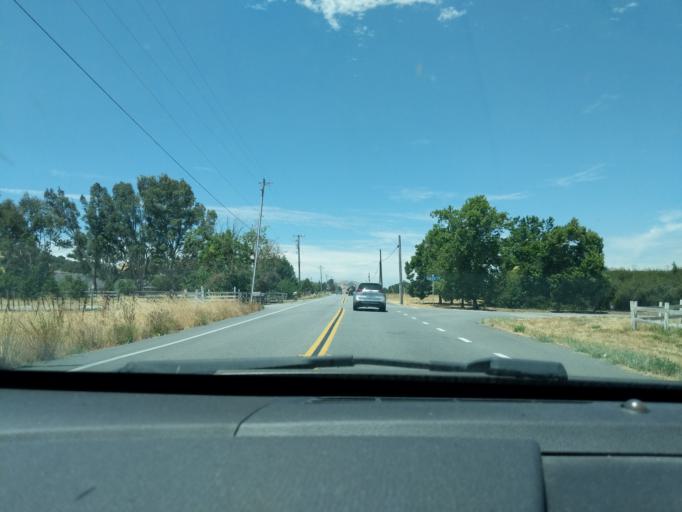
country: US
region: California
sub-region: Santa Clara County
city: Morgan Hill
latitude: 37.1521
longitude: -121.6839
